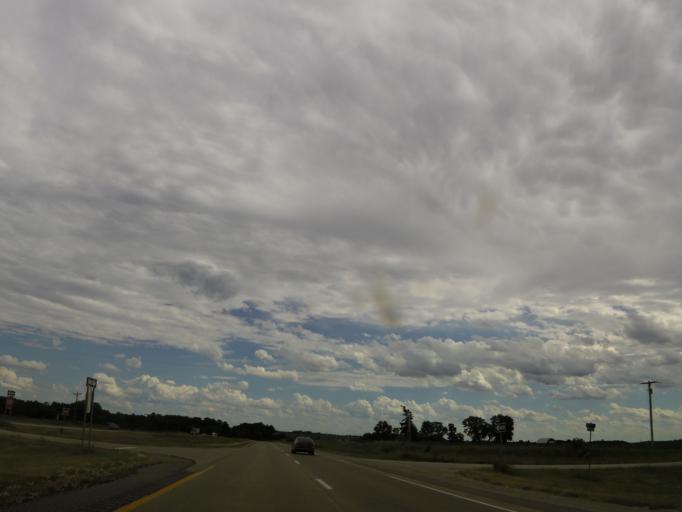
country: US
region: Iowa
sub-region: Henry County
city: Mount Pleasant
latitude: 41.0472
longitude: -91.5447
